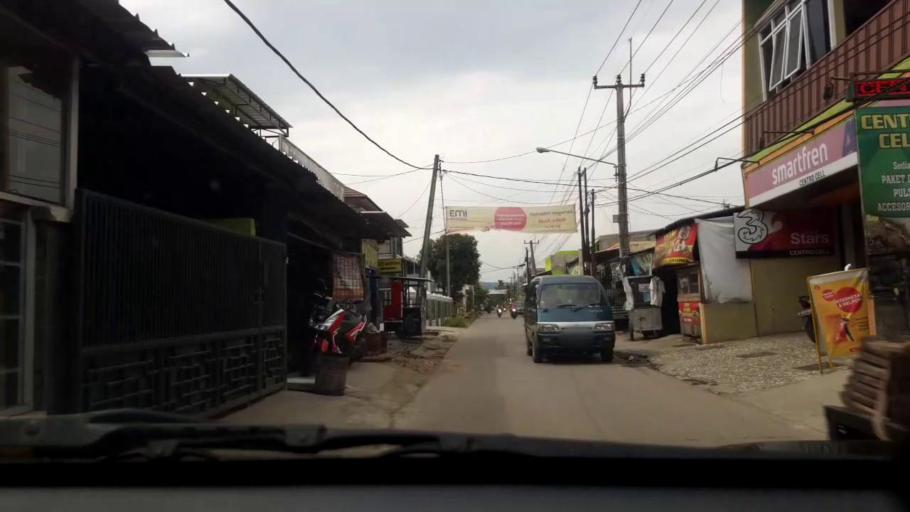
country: ID
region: West Java
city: Cileunyi
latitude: -6.9460
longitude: 107.7204
